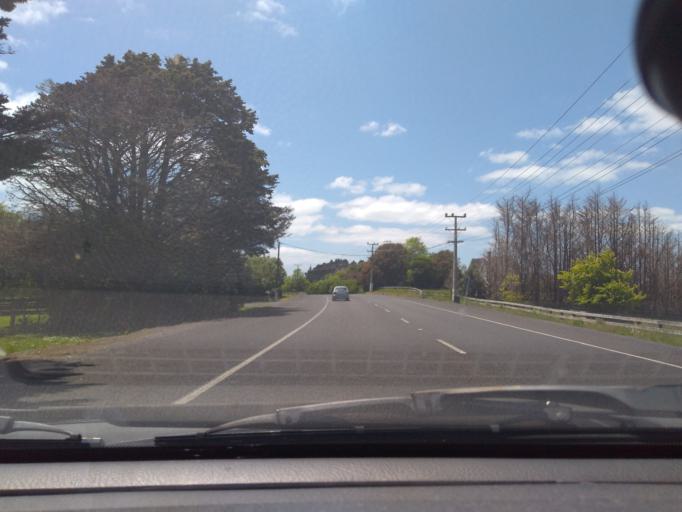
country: NZ
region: Auckland
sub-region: Auckland
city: Pakuranga
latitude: -36.9056
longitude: 175.0063
